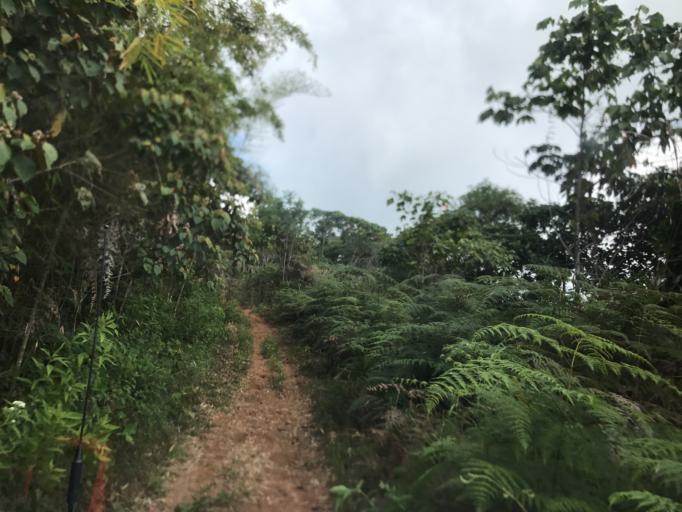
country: CO
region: Valle del Cauca
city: Obando
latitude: 4.5776
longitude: -75.8909
